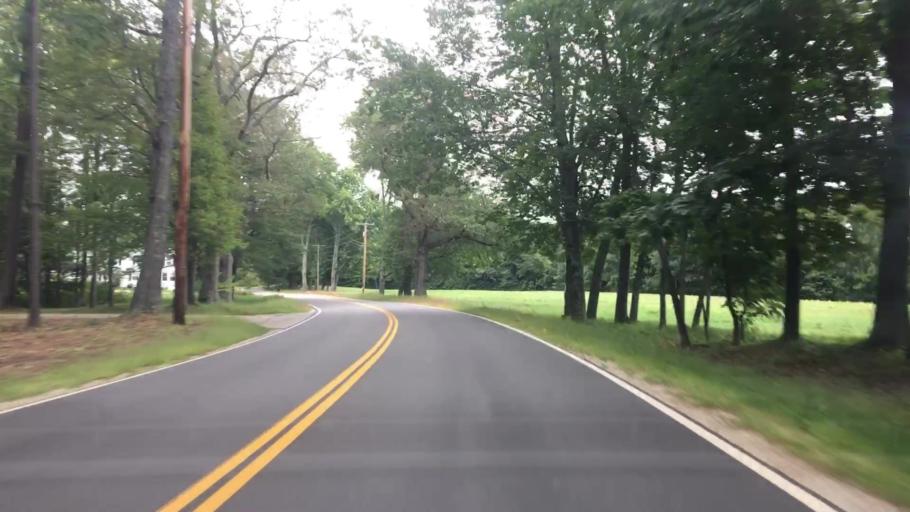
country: US
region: Maine
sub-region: Cumberland County
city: New Gloucester
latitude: 43.9042
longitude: -70.2512
